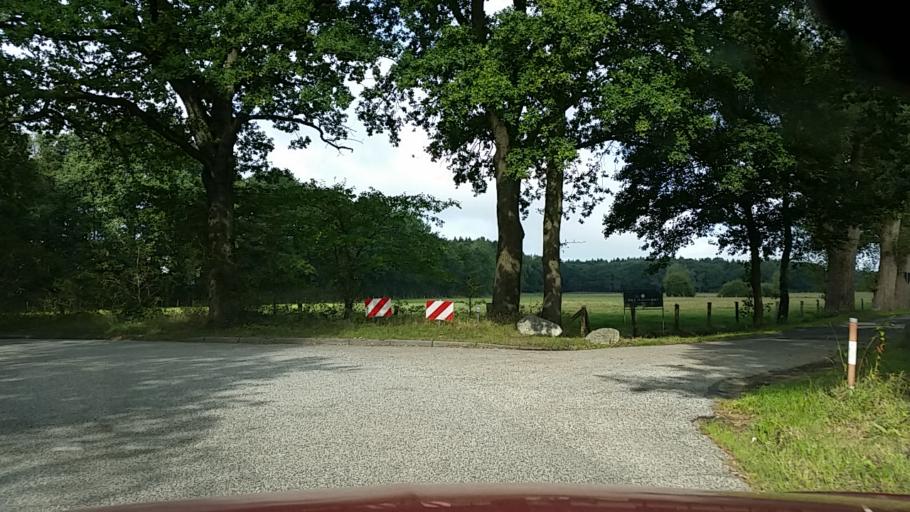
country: DE
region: Schleswig-Holstein
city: Wedel
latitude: 53.5987
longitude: 9.7362
